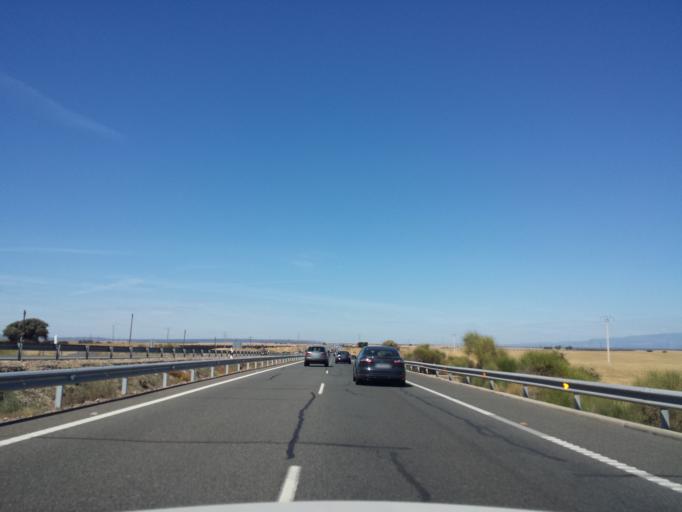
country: ES
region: Castille-La Mancha
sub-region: Province of Toledo
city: Caleruela
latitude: 39.8953
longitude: -5.3049
